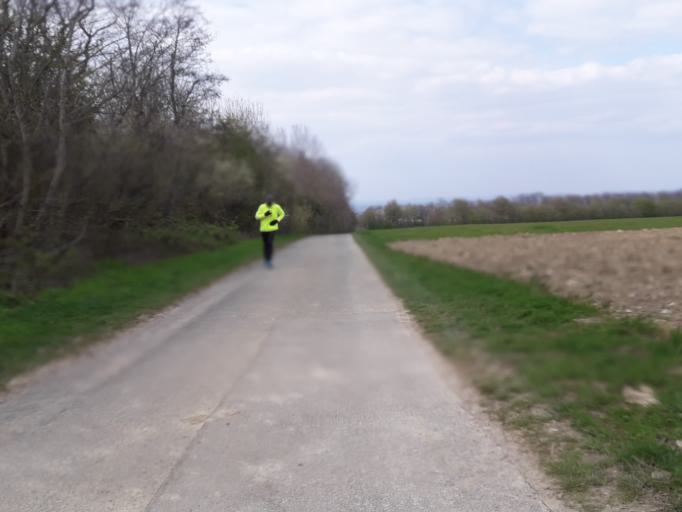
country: DE
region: North Rhine-Westphalia
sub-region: Regierungsbezirk Detmold
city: Paderborn
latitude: 51.6916
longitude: 8.7640
